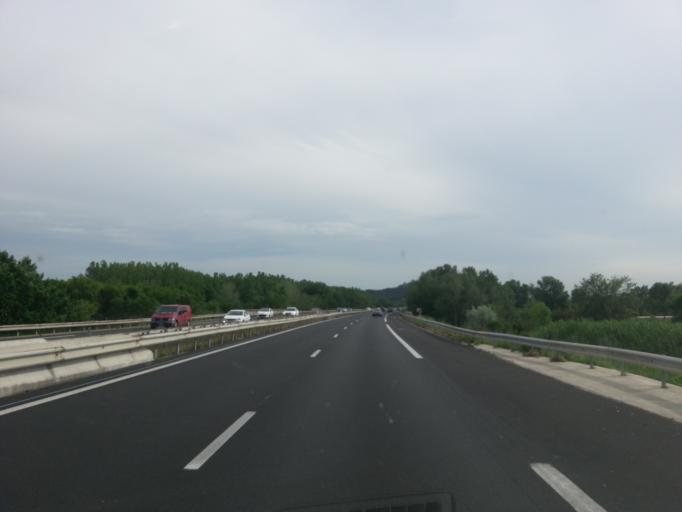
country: FR
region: Provence-Alpes-Cote d'Azur
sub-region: Departement du Vaucluse
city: Caderousse
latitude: 44.0979
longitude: 4.7883
